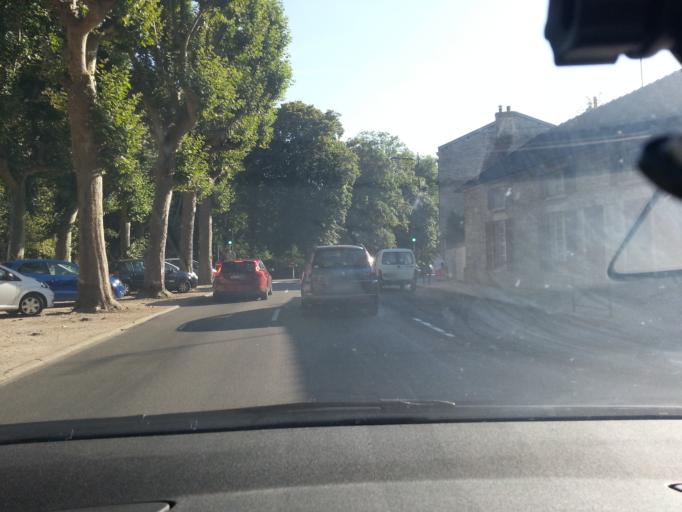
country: FR
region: Bourgogne
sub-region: Departement de la Cote-d'Or
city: Beaune
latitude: 47.0267
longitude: 4.8360
